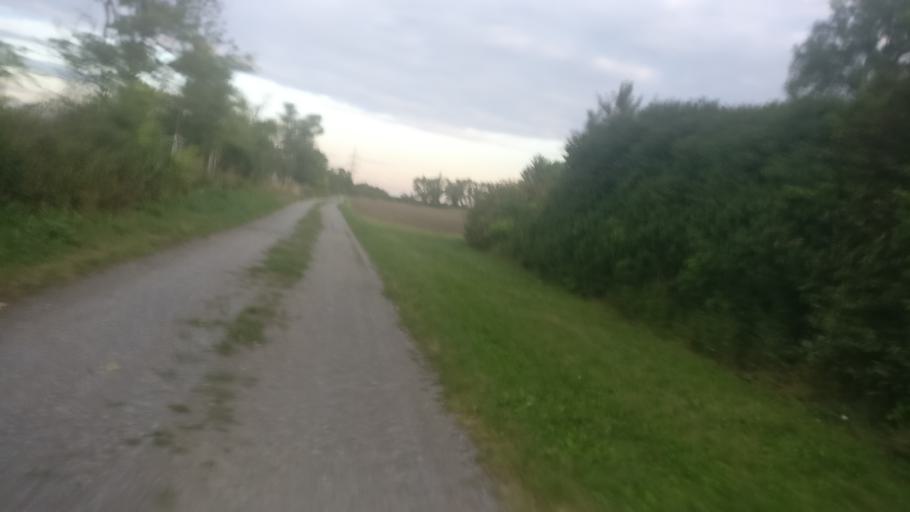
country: AT
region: Lower Austria
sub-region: Politischer Bezirk Modling
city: Munchendorf
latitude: 48.0176
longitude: 16.3773
